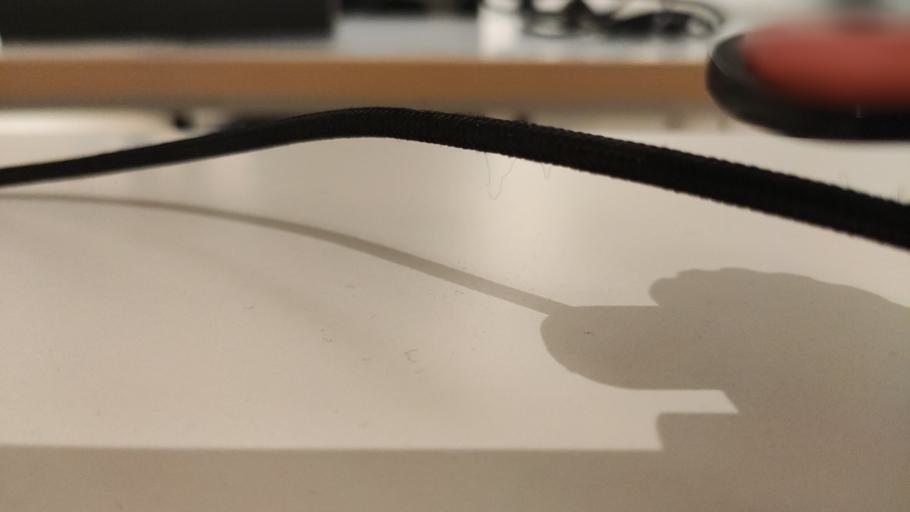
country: RU
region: Moskovskaya
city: Dorokhovo
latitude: 55.5026
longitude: 36.3463
